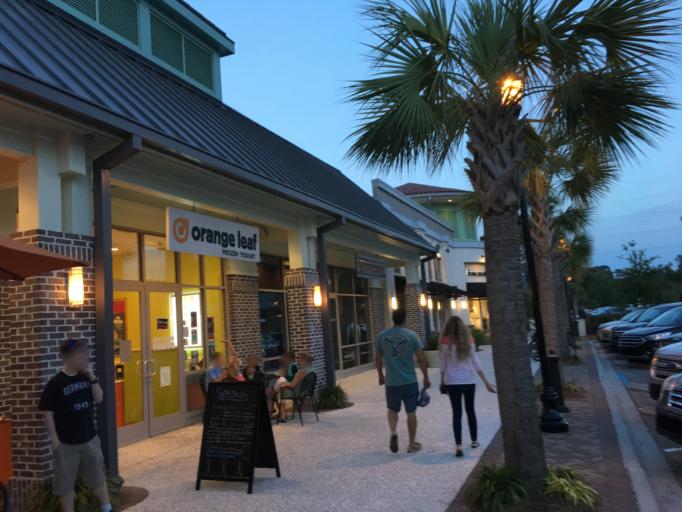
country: US
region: South Carolina
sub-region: Beaufort County
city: Hilton Head Island
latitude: 32.1854
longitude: -80.7212
